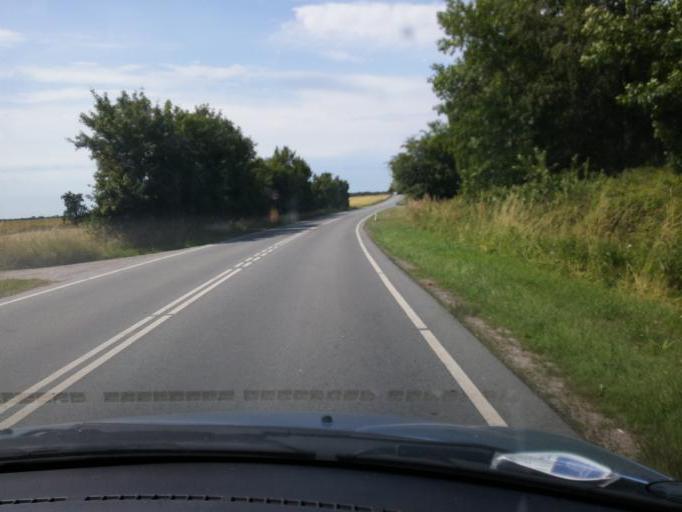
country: DK
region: South Denmark
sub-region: Kerteminde Kommune
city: Langeskov
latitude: 55.4075
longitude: 10.5935
